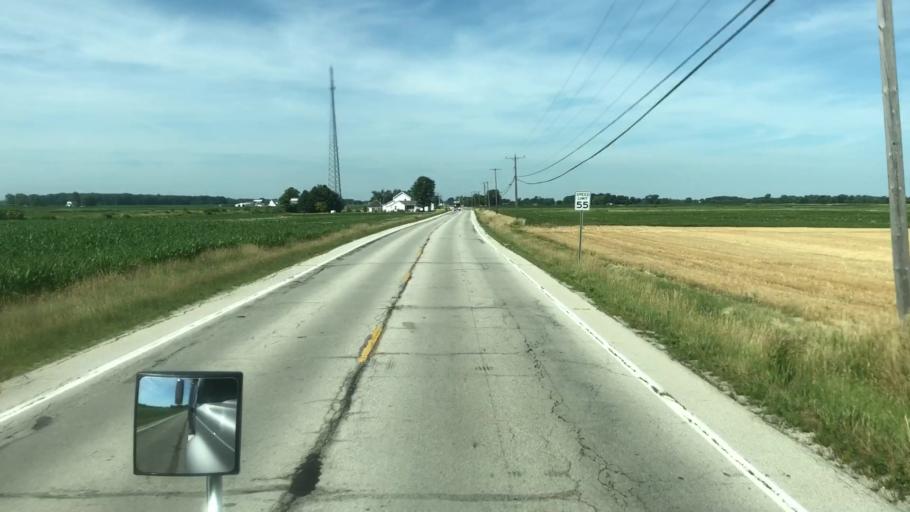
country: US
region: Ohio
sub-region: Ottawa County
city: Port Clinton
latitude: 41.4297
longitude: -82.8515
